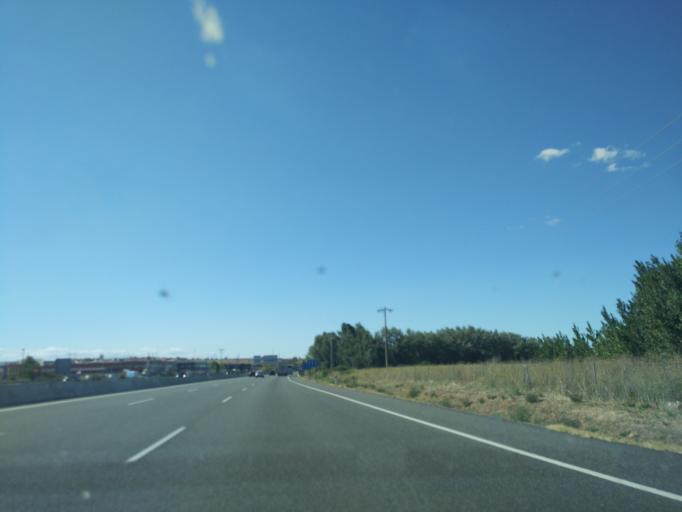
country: ES
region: Castille and Leon
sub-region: Provincia de Zamora
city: Benavente
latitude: 42.0011
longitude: -5.6573
